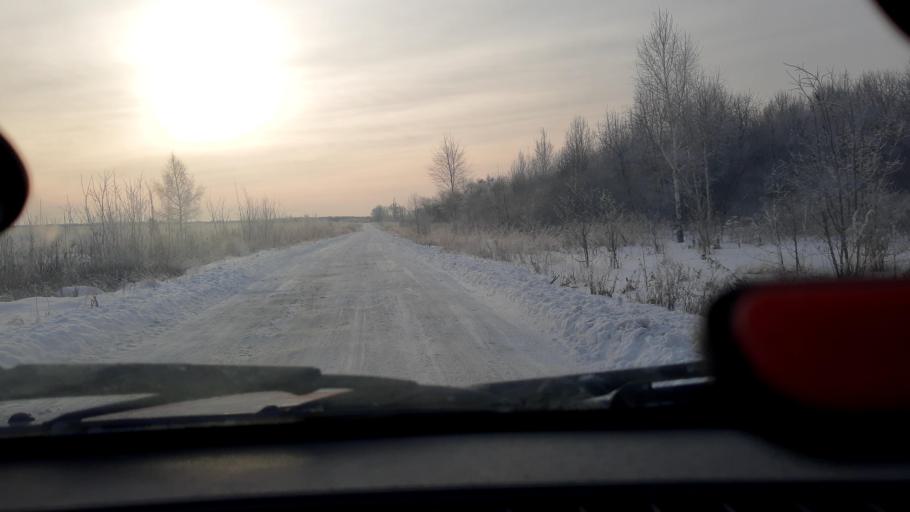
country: RU
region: Bashkortostan
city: Iglino
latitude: 54.7383
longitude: 56.2430
